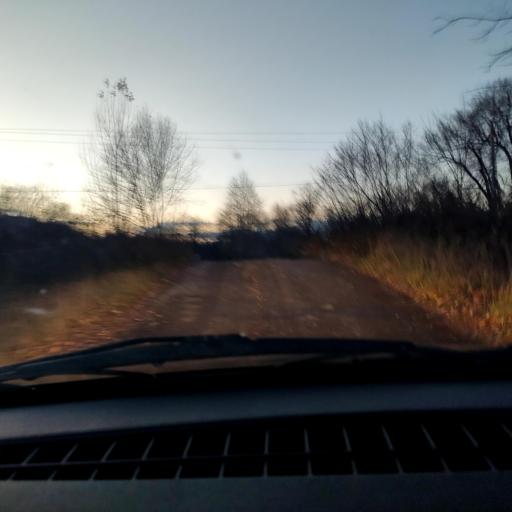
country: RU
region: Bashkortostan
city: Ufa
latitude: 54.6551
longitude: 55.8878
